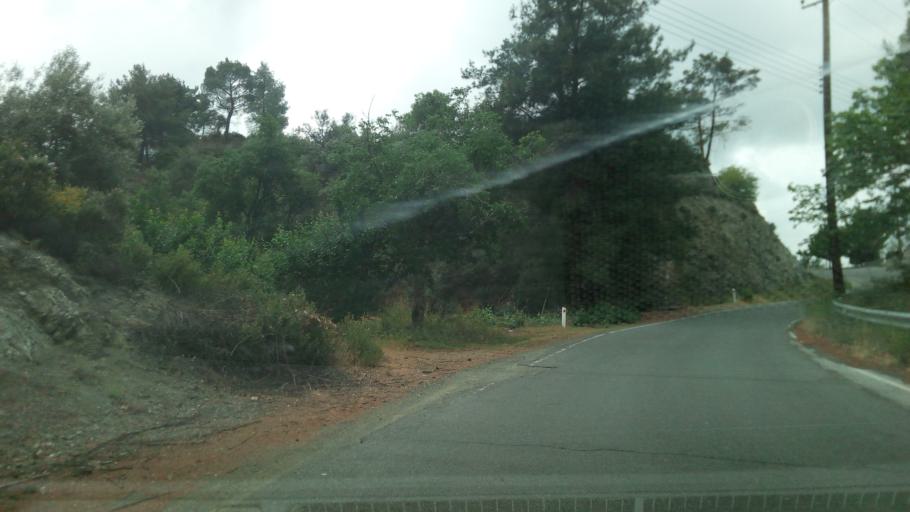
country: CY
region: Limassol
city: Pelendri
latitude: 34.9006
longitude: 32.9930
